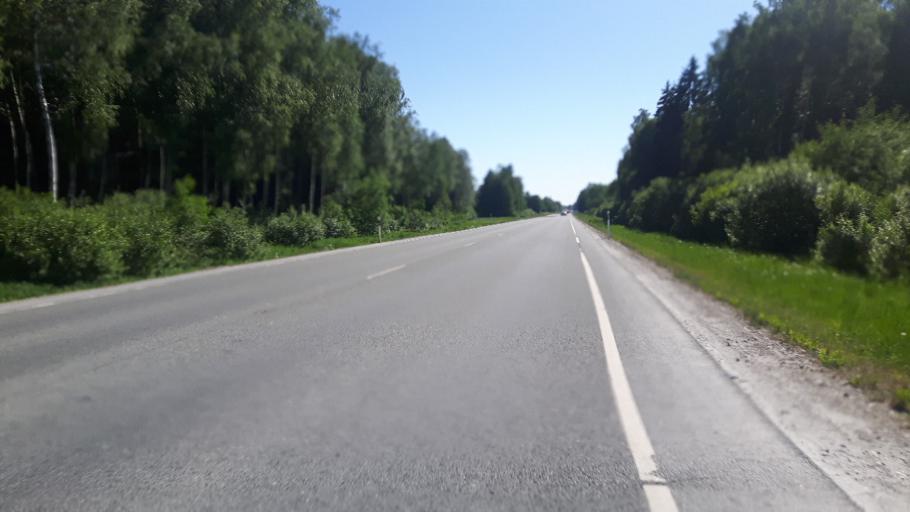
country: EE
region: Raplamaa
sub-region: Rapla vald
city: Rapla
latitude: 59.0222
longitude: 24.8104
